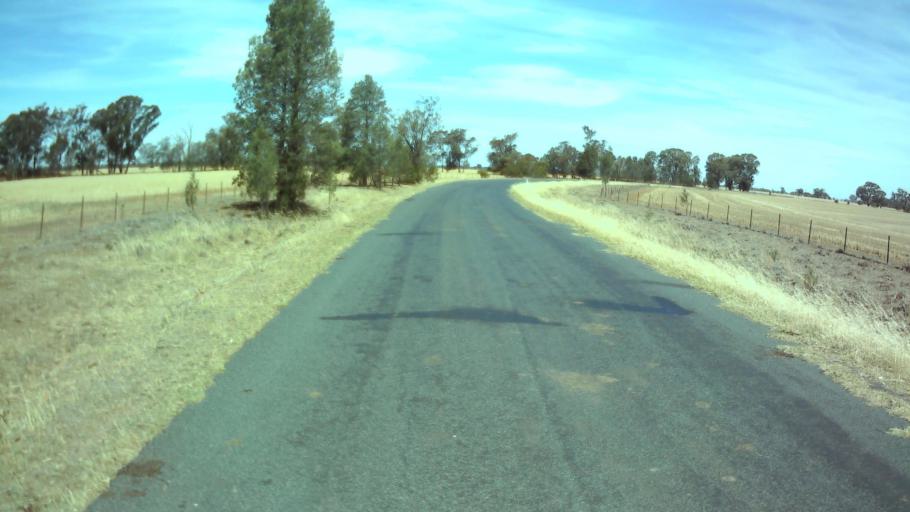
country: AU
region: New South Wales
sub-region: Weddin
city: Grenfell
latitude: -33.9579
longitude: 147.7798
